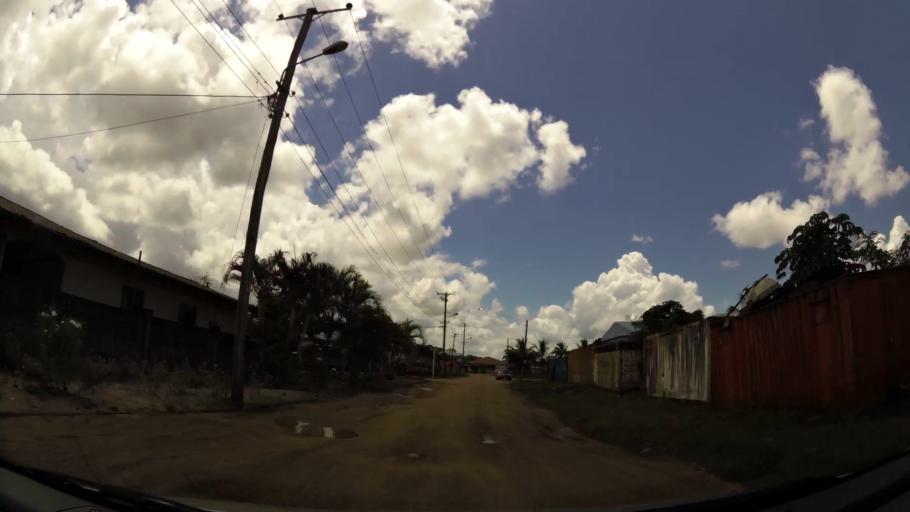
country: SR
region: Paramaribo
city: Paramaribo
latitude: 5.8637
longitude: -55.1675
